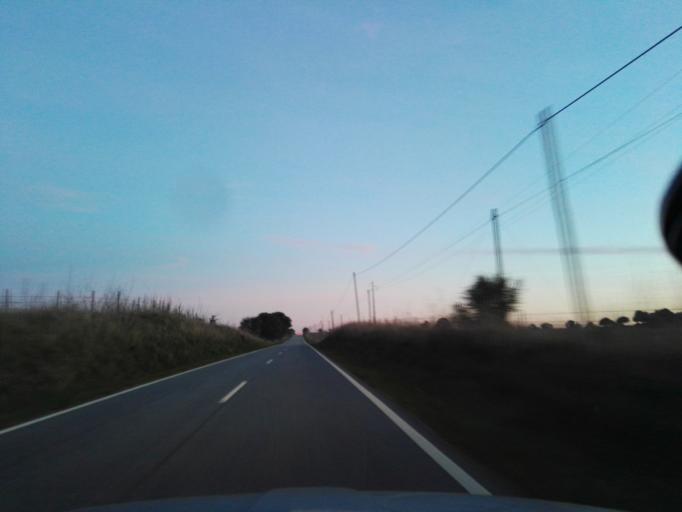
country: PT
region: Evora
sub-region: Arraiolos
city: Arraiolos
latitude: 38.7156
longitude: -8.0478
